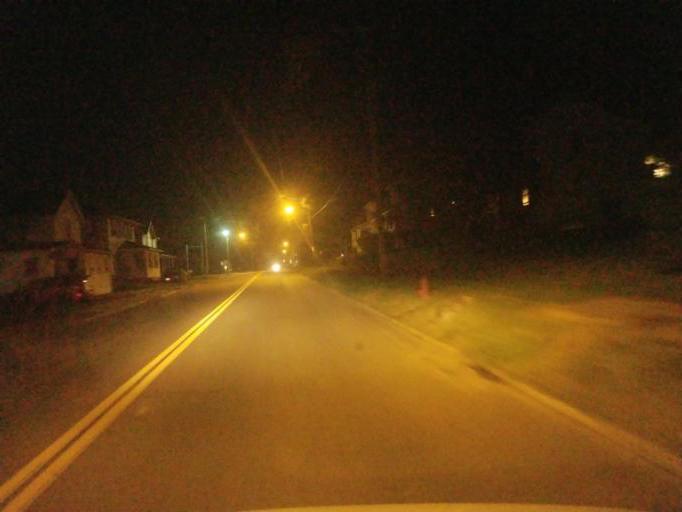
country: US
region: Ohio
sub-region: Stark County
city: Minerva
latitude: 40.7309
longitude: -81.1093
